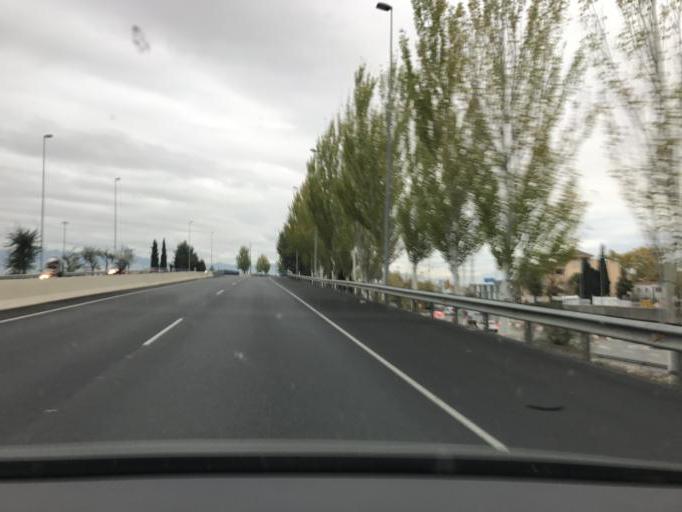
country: ES
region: Andalusia
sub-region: Provincia de Granada
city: Maracena
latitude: 37.2118
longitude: -3.6239
